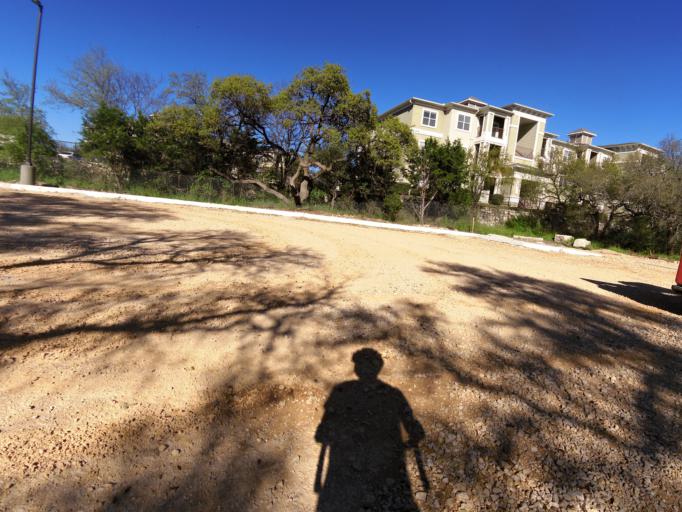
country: US
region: Texas
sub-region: Bexar County
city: Shavano Park
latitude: 29.6006
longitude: -98.5984
